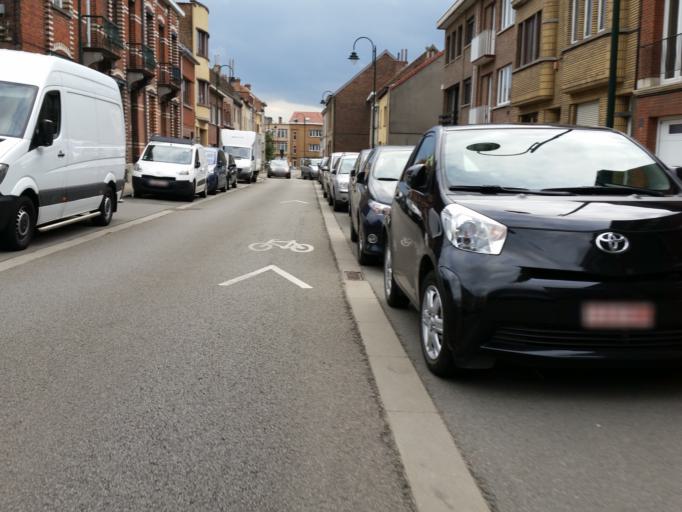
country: BE
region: Flanders
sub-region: Provincie Vlaams-Brabant
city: Diegem
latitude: 50.8933
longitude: 4.4193
